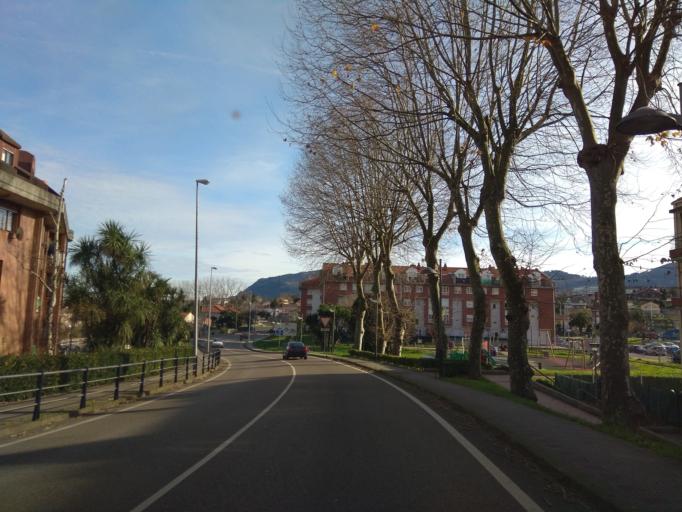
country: ES
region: Cantabria
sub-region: Provincia de Cantabria
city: El Astillero
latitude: 43.4060
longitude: -3.8400
